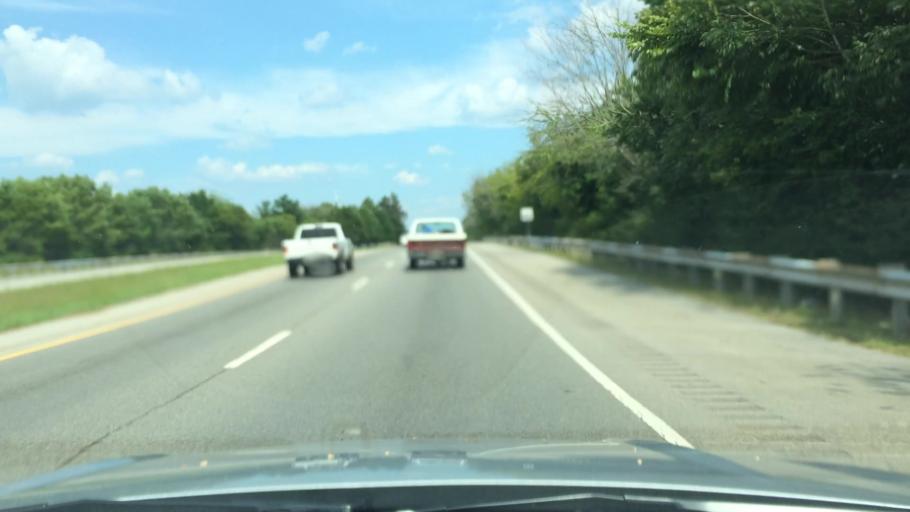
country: US
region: Tennessee
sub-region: Blount County
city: Maryville
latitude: 35.7560
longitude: -84.0325
